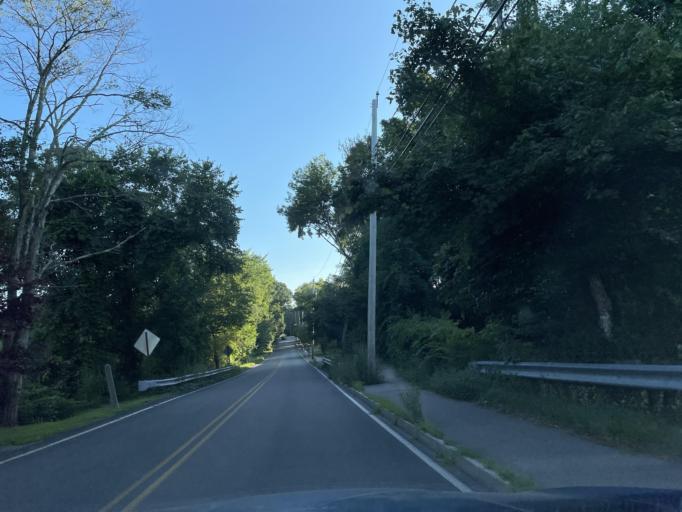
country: US
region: Massachusetts
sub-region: Plymouth County
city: Bridgewater
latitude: 41.9949
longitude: -70.9538
